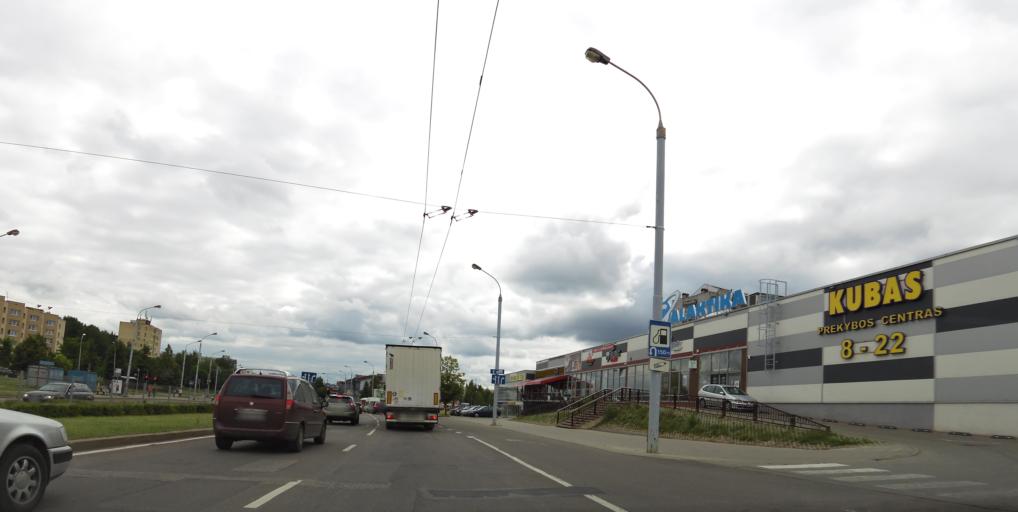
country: LT
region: Vilnius County
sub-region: Vilnius
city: Fabijoniskes
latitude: 54.7273
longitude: 25.2337
